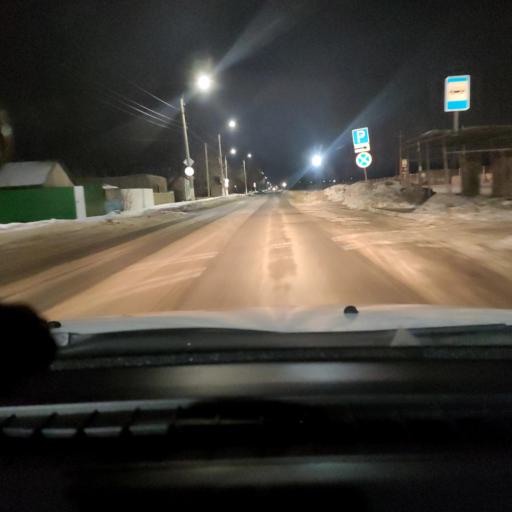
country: RU
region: Samara
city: Chapayevsk
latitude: 52.9784
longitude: 49.7024
